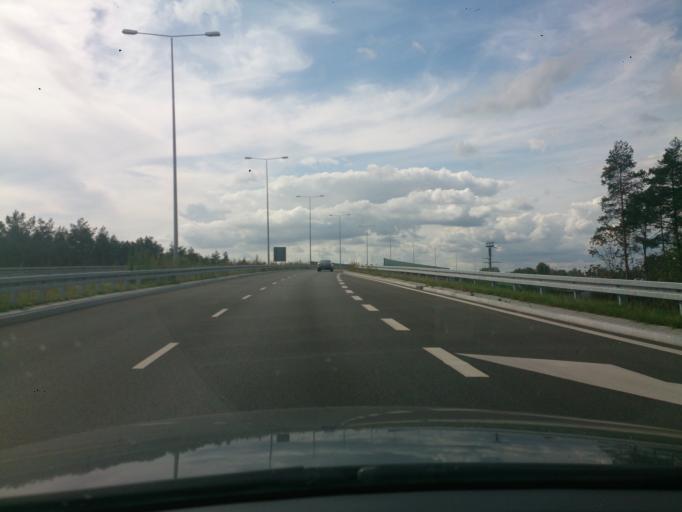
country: PL
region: Kujawsko-Pomorskie
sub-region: Grudziadz
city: Grudziadz
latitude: 53.4477
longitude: 18.7319
